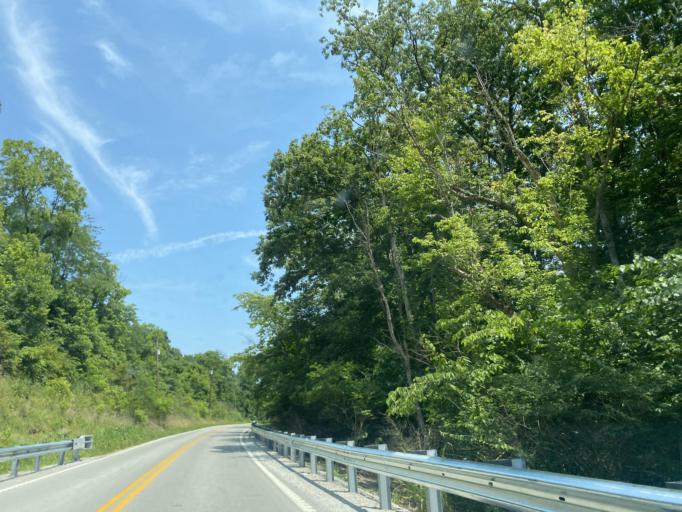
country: US
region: Kentucky
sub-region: Campbell County
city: Claryville
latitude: 38.8917
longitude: -84.4478
